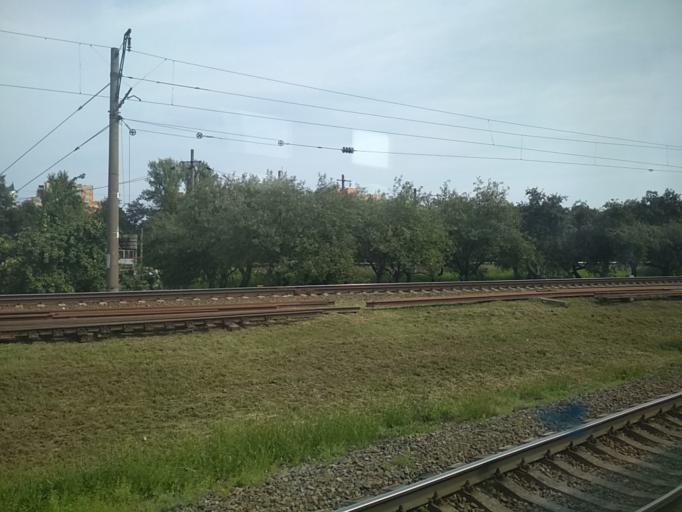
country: BY
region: Minsk
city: Minsk
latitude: 53.8877
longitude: 27.5594
